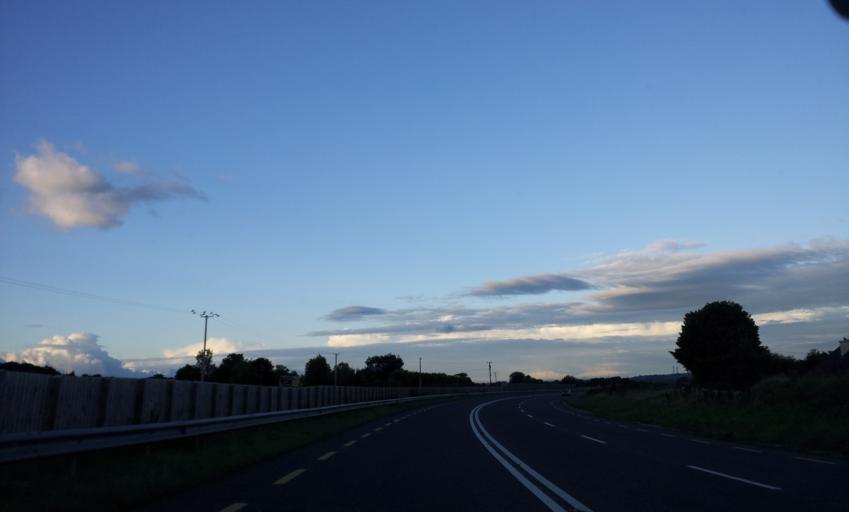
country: IE
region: Munster
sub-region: County Limerick
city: Newcastle West
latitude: 52.4340
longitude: -9.1252
